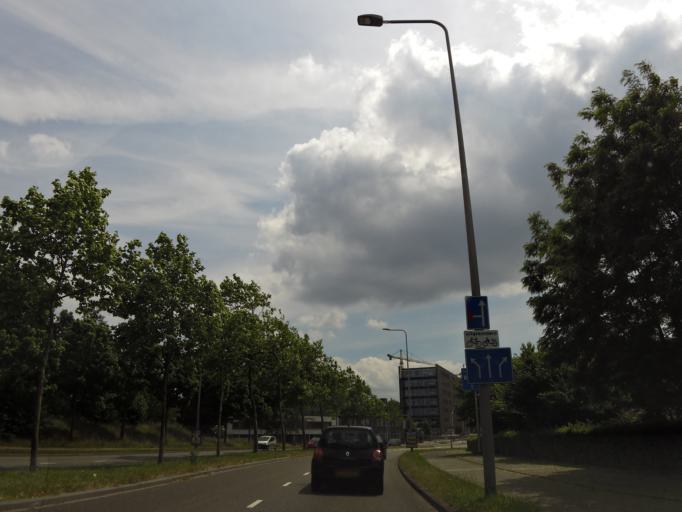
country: NL
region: Limburg
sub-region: Gemeente Heerlen
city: Heerlen
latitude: 50.8951
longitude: 5.9706
